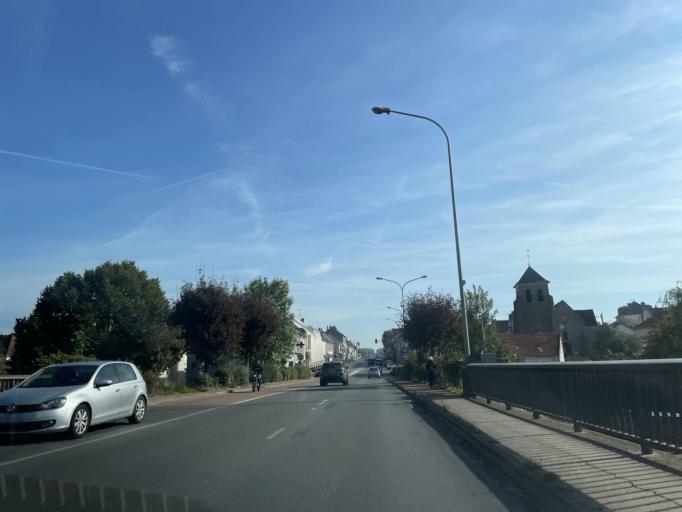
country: FR
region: Ile-de-France
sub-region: Departement de Seine-et-Marne
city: Trilport
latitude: 48.9577
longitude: 2.9445
